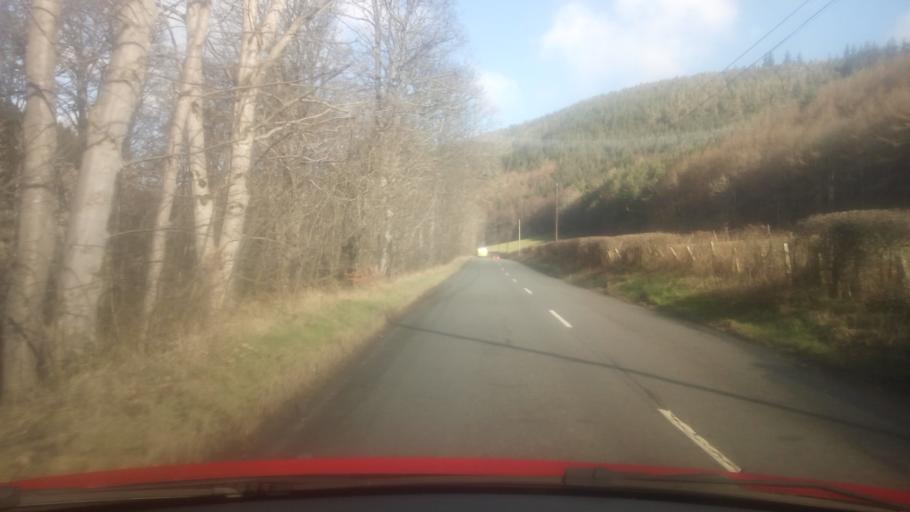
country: GB
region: Scotland
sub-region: The Scottish Borders
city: Selkirk
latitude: 55.5939
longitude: -2.8666
